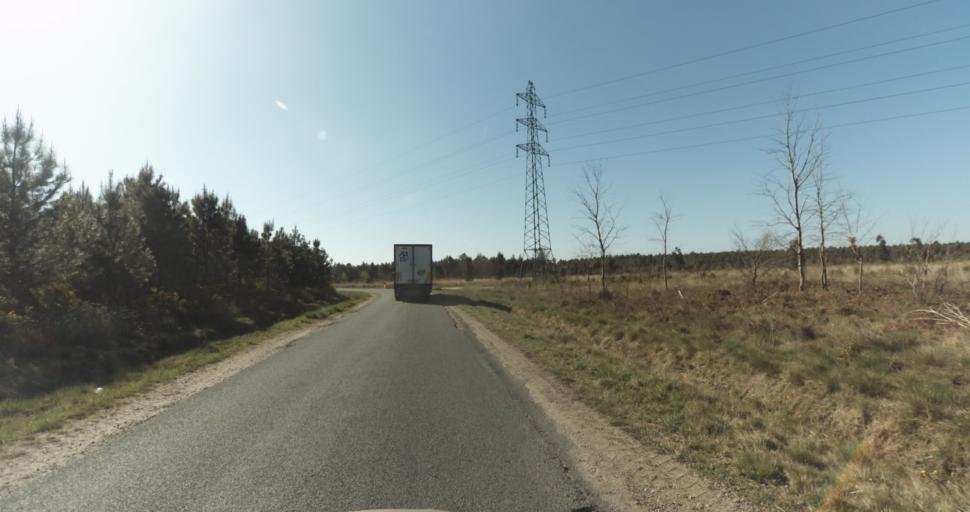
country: FR
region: Aquitaine
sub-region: Departement de la Gironde
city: Marcheprime
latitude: 44.7515
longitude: -0.8483
